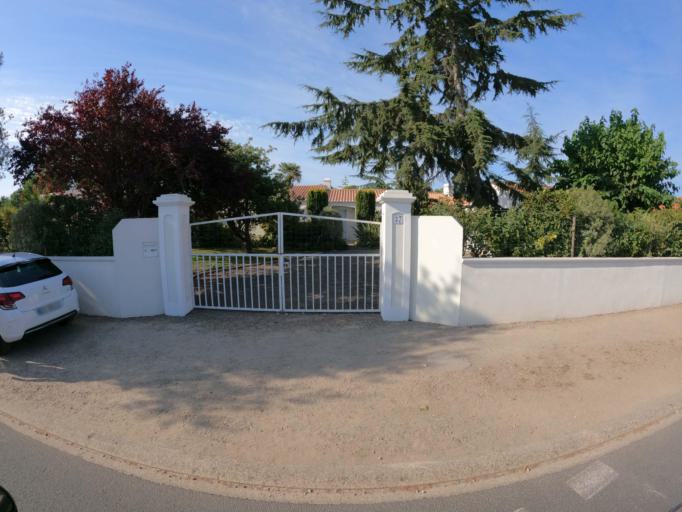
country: FR
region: Pays de la Loire
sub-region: Departement de la Vendee
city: Saint-Jean-de-Monts
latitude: 46.7989
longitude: -2.0739
